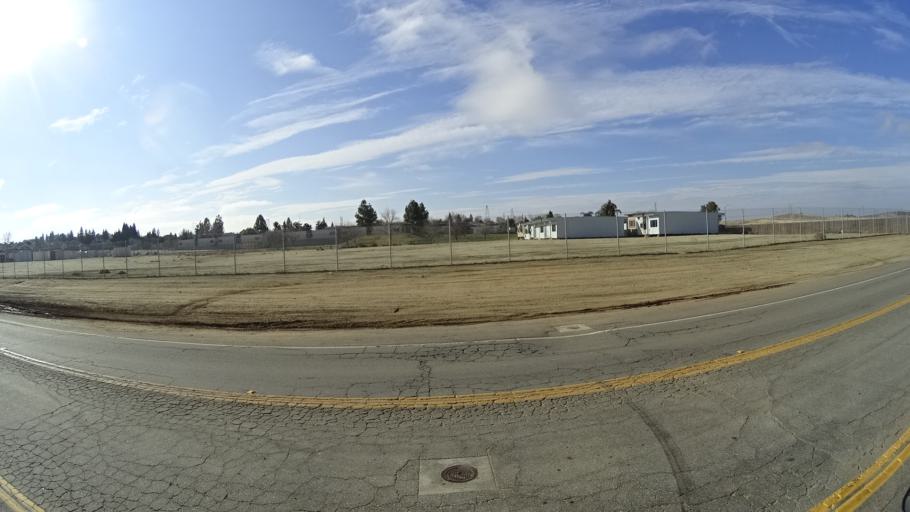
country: US
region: California
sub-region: Kern County
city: Oildale
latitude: 35.4050
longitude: -118.9143
